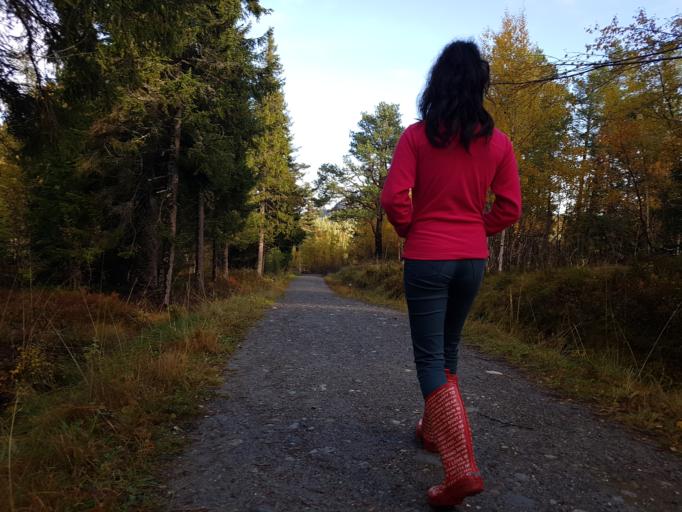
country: NO
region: Sor-Trondelag
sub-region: Trondheim
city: Trondheim
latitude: 63.4192
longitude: 10.2822
